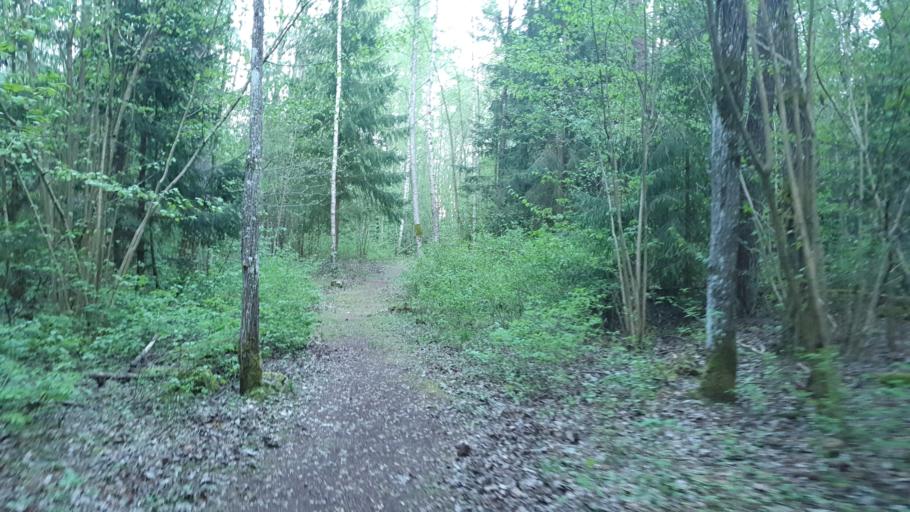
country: LV
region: Ikskile
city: Ikskile
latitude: 56.8350
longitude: 24.4399
